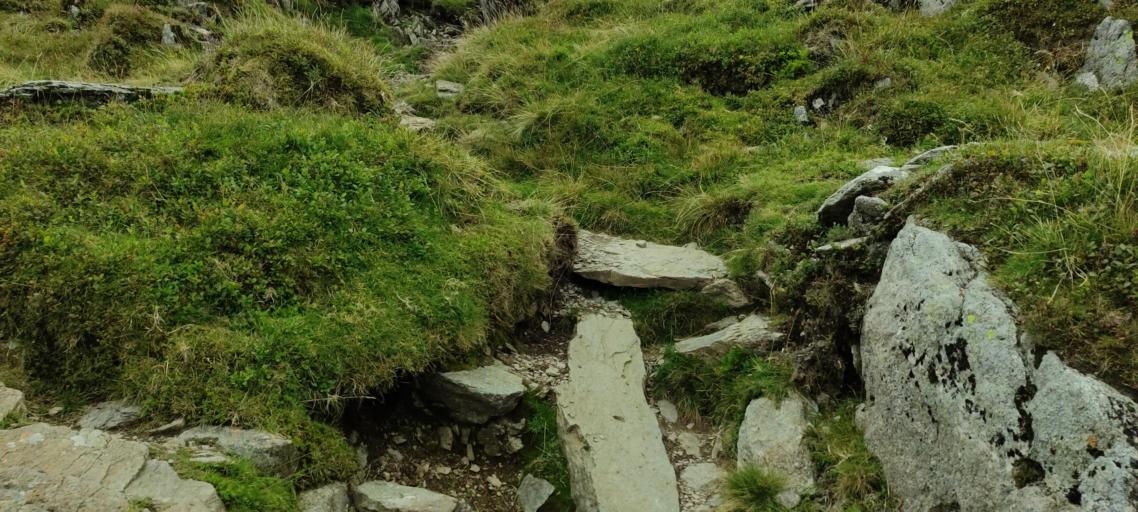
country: GB
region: England
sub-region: Cumbria
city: Ambleside
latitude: 54.5171
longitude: -2.9711
